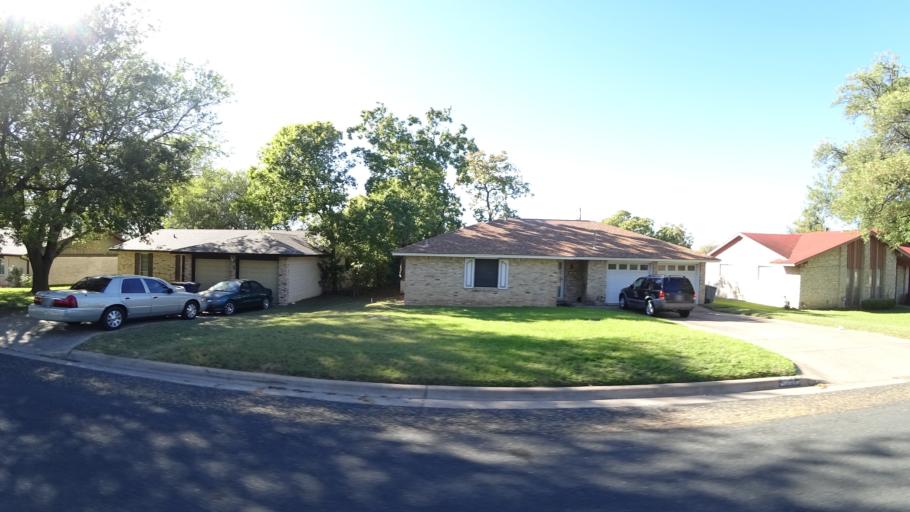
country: US
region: Texas
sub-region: Travis County
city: Austin
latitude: 30.2886
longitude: -97.6740
